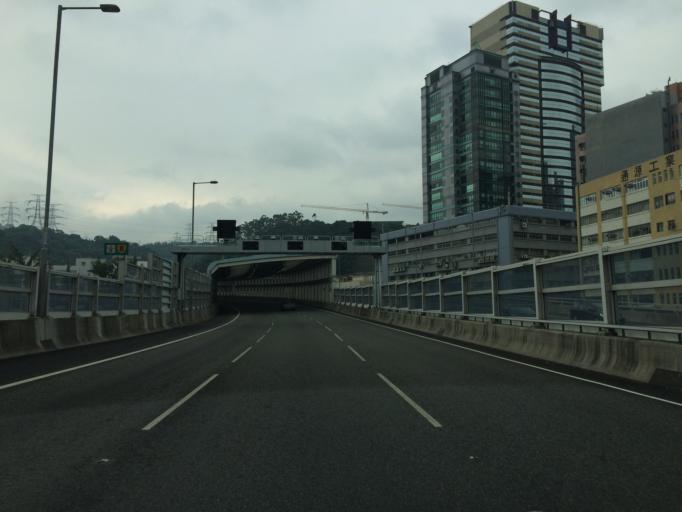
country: HK
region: Sham Shui Po
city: Sham Shui Po
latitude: 22.3363
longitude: 114.1446
